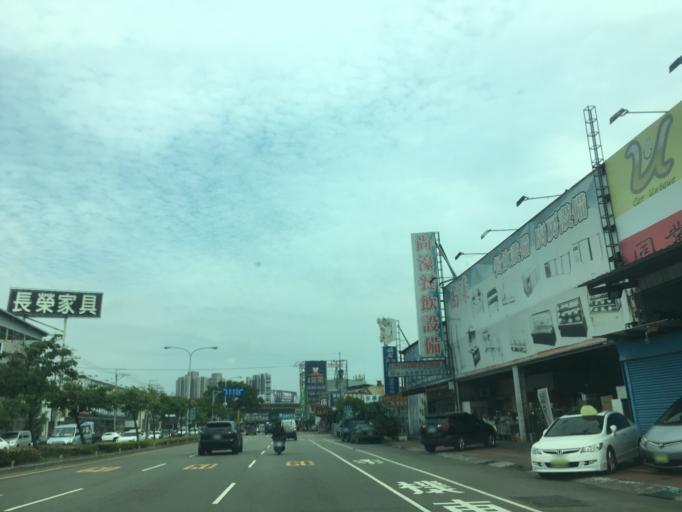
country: TW
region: Taiwan
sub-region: Taichung City
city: Taichung
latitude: 24.1034
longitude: 120.6697
